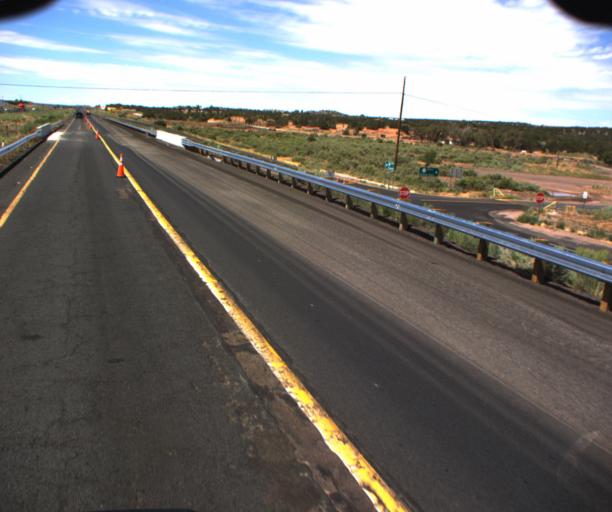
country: US
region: Arizona
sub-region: Apache County
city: Houck
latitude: 35.3385
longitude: -109.0679
